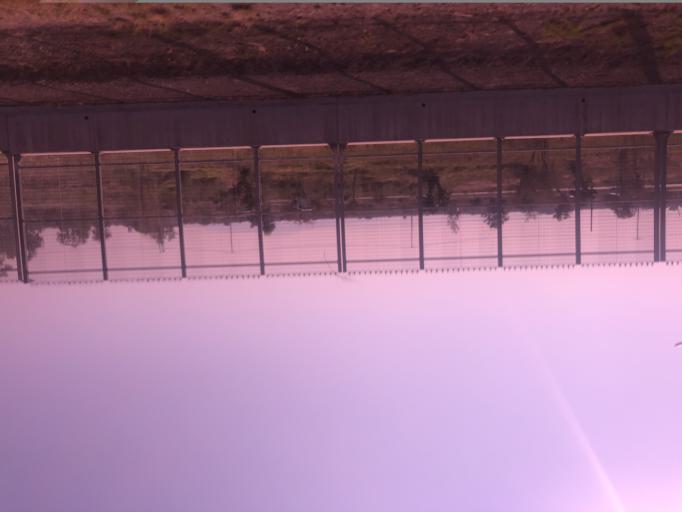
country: MX
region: Mexico
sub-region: Ciudad Nezahualcoyotl
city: Poligonos
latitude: 19.4791
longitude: -98.9802
